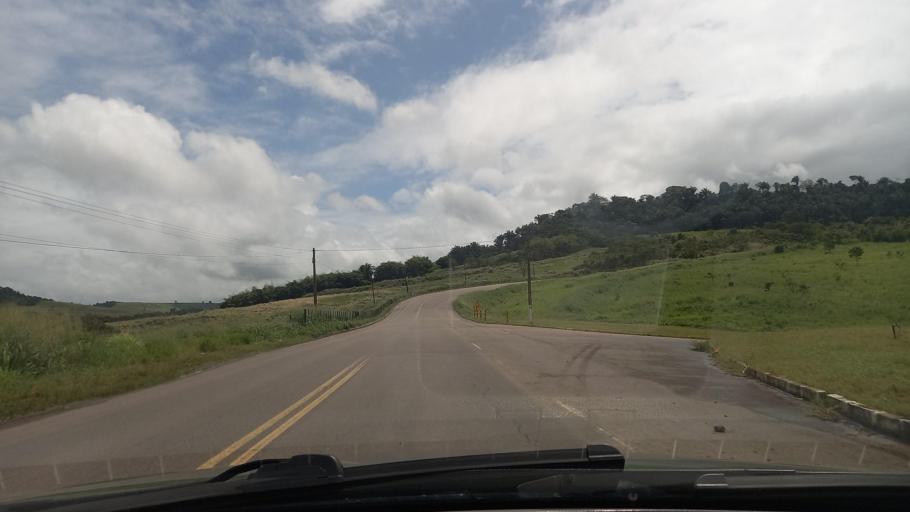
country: BR
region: Alagoas
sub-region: Sao Miguel Dos Campos
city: Sao Miguel dos Campos
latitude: -9.8138
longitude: -36.2212
